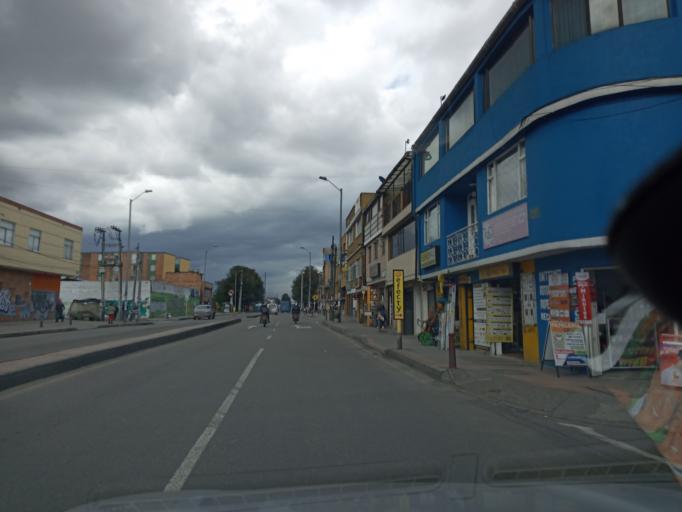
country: CO
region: Cundinamarca
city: Funza
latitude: 4.6830
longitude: -74.1325
